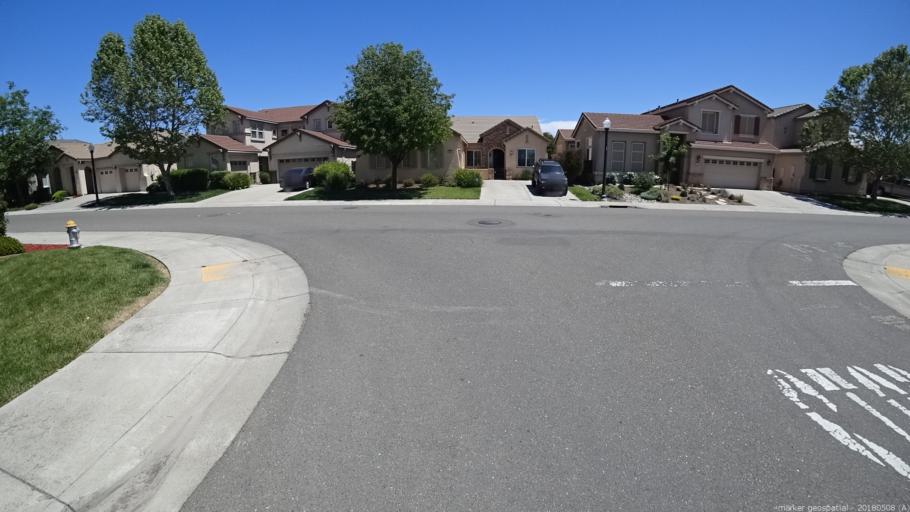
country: US
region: California
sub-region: Sacramento County
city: Elverta
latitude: 38.6825
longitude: -121.5299
